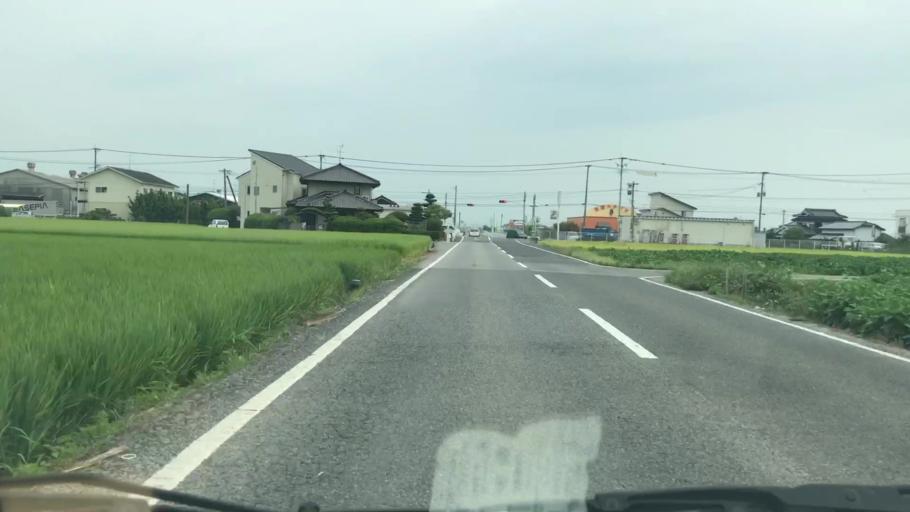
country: JP
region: Saga Prefecture
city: Saga-shi
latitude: 33.2279
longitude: 130.2926
